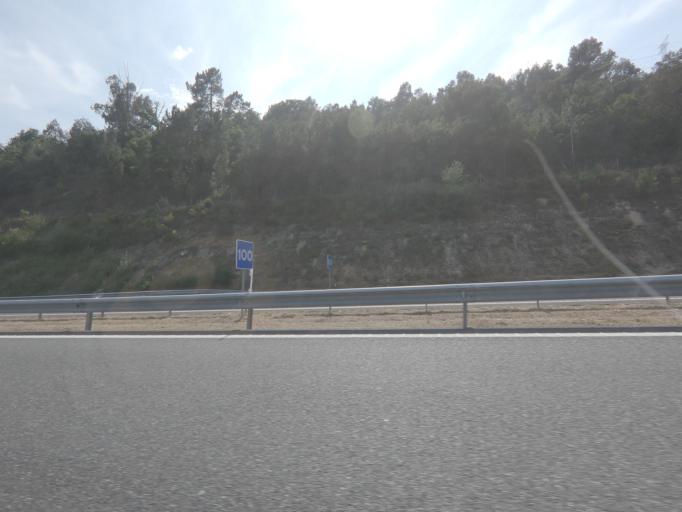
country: ES
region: Galicia
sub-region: Provincia de Ourense
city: Cenlle
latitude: 42.3246
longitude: -8.0770
